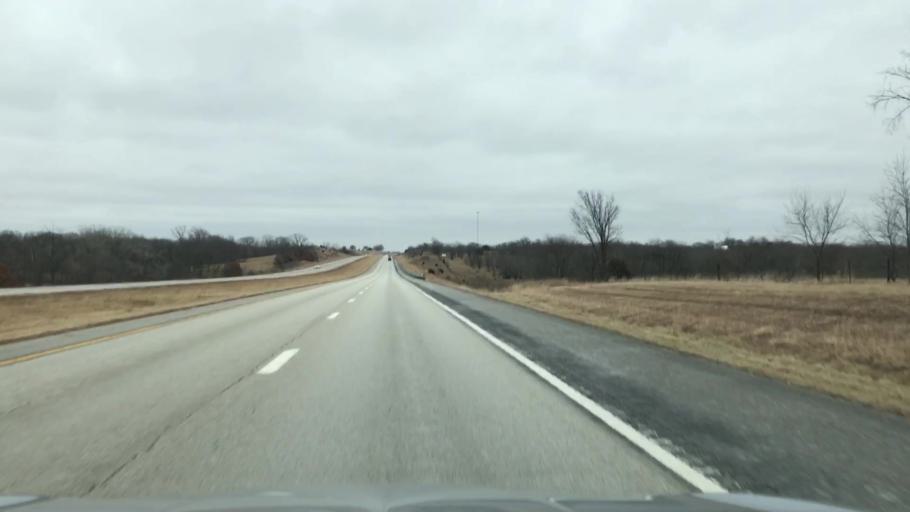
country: US
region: Missouri
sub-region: Caldwell County
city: Hamilton
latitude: 39.7493
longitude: -94.0742
